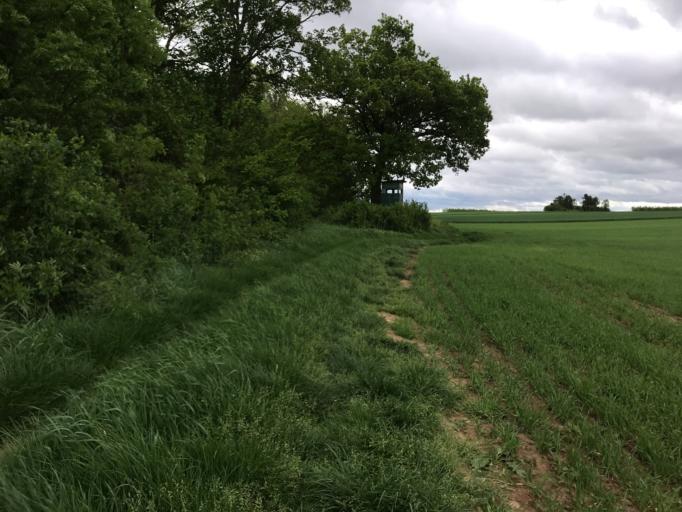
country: DE
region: Rheinland-Pfalz
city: Essenheim
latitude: 49.9531
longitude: 8.1644
